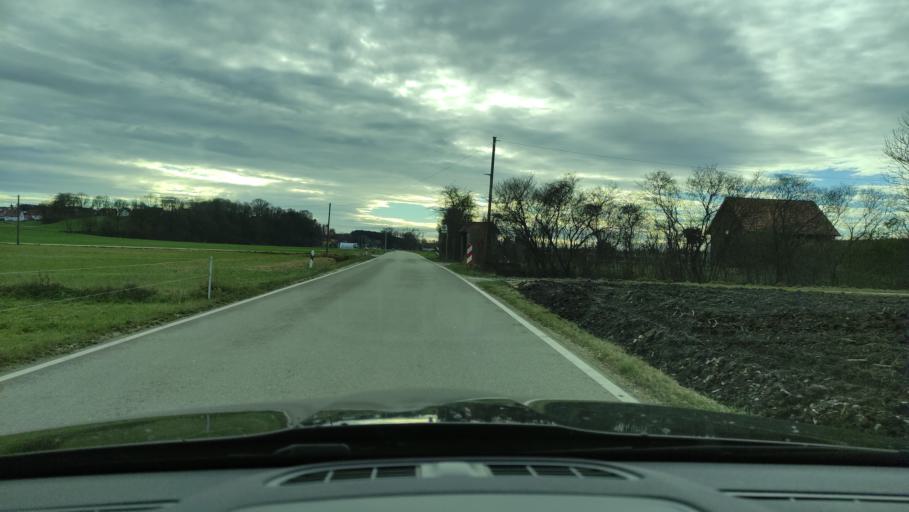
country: DE
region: Bavaria
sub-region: Swabia
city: Deisenhausen
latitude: 48.2653
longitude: 10.3251
